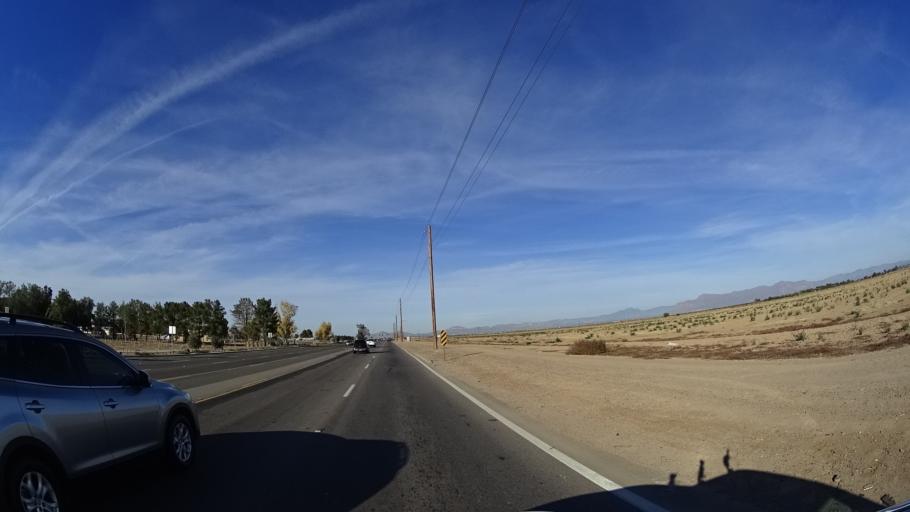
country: US
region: Arizona
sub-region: Maricopa County
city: Queen Creek
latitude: 33.2728
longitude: -111.6348
